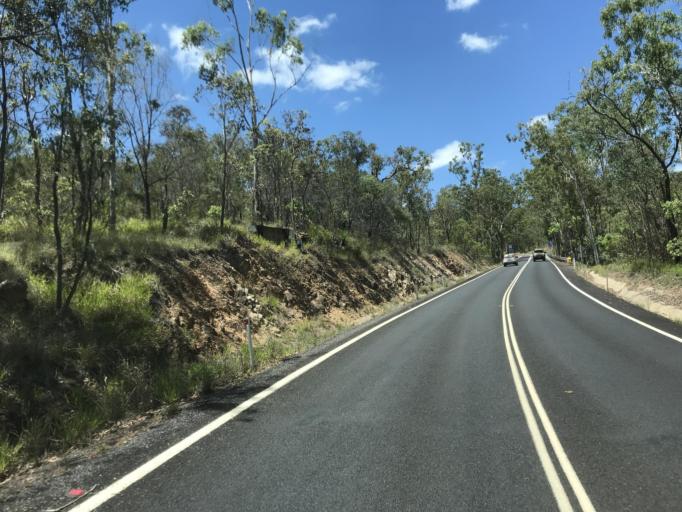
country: AU
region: Queensland
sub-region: Tablelands
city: Atherton
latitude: -17.4014
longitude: 145.3898
